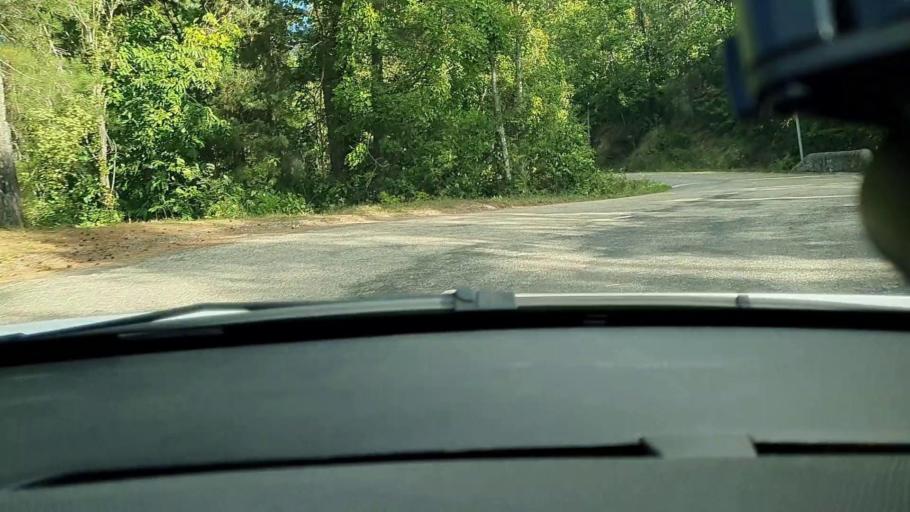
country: FR
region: Languedoc-Roussillon
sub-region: Departement du Gard
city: Besseges
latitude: 44.3896
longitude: 3.9941
